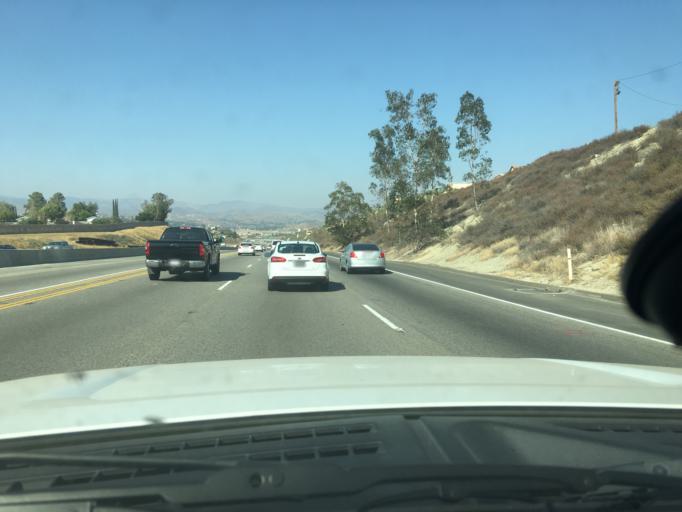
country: US
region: California
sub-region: Los Angeles County
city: Santa Clarita
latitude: 34.3923
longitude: -118.4727
